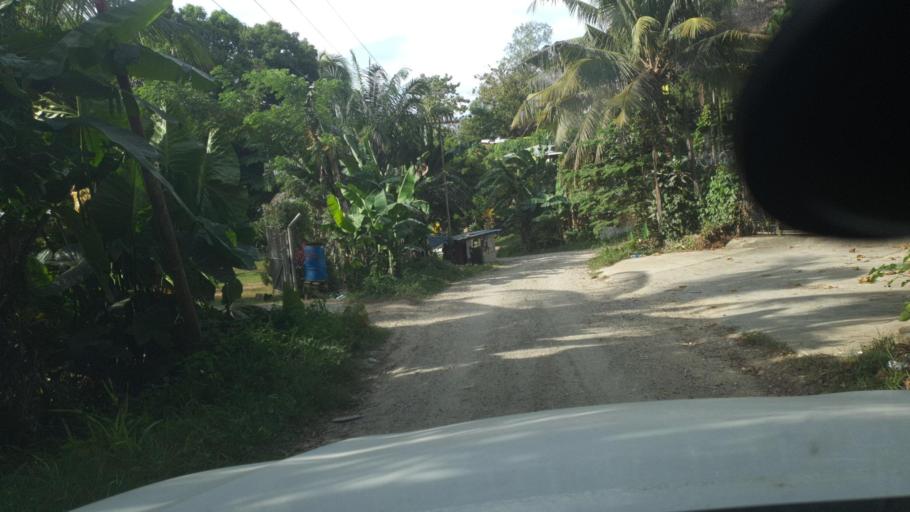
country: SB
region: Guadalcanal
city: Honiara
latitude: -9.4392
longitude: 159.9421
